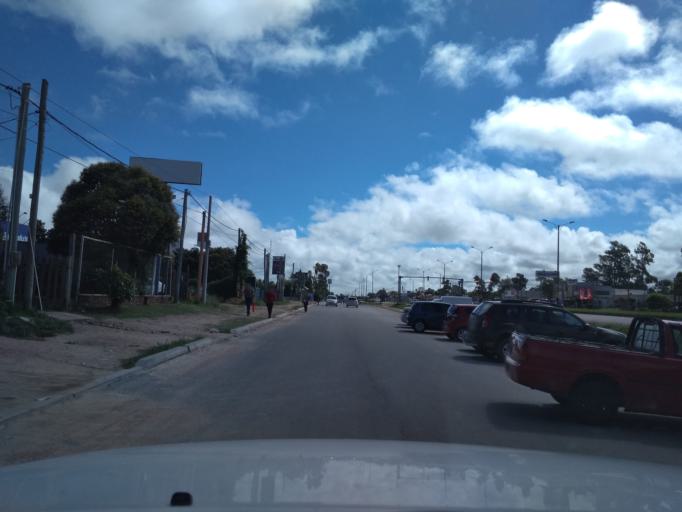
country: UY
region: Canelones
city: Barra de Carrasco
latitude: -34.8309
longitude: -55.9742
